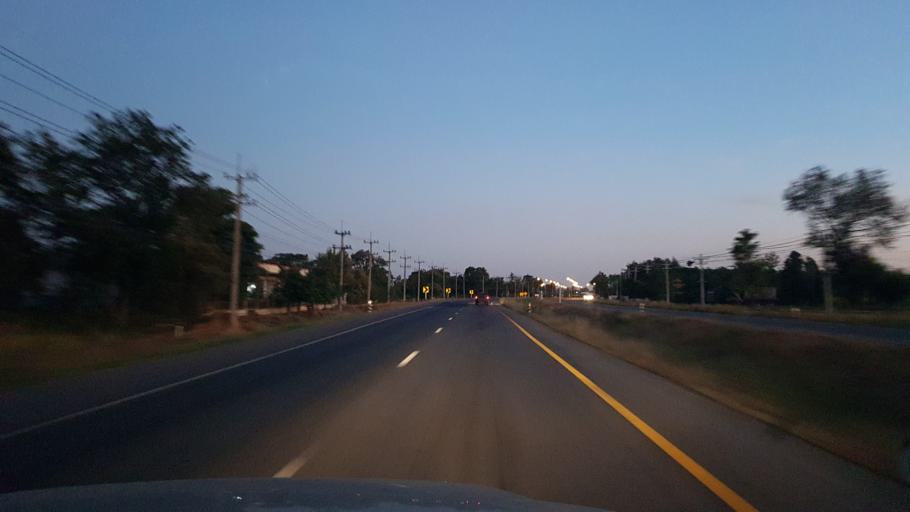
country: TH
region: Chaiyaphum
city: Phu Khiao
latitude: 16.3052
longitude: 102.2061
